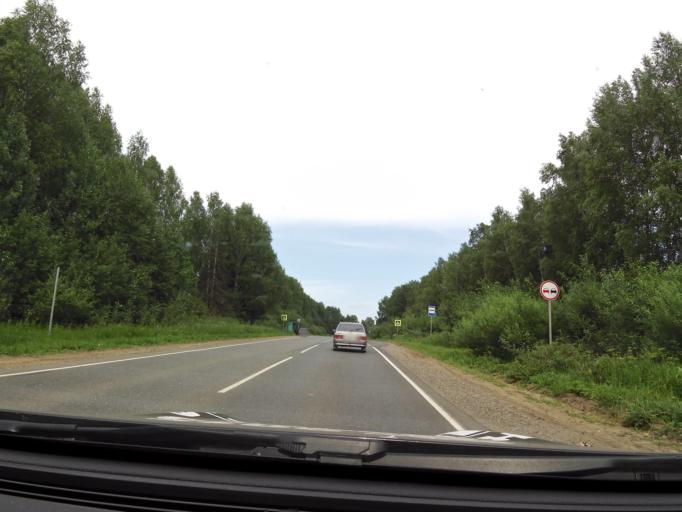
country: RU
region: Kirov
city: Vakhrushi
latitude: 58.6457
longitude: 49.8592
